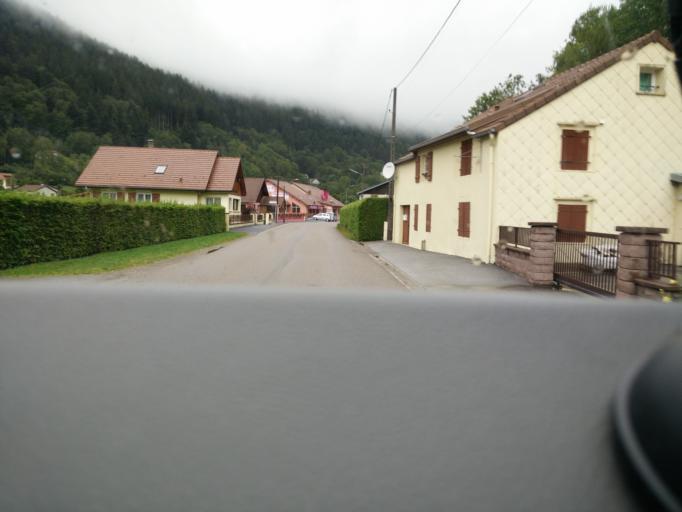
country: FR
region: Lorraine
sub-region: Departement des Vosges
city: Plainfaing
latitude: 48.1460
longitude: 7.0128
